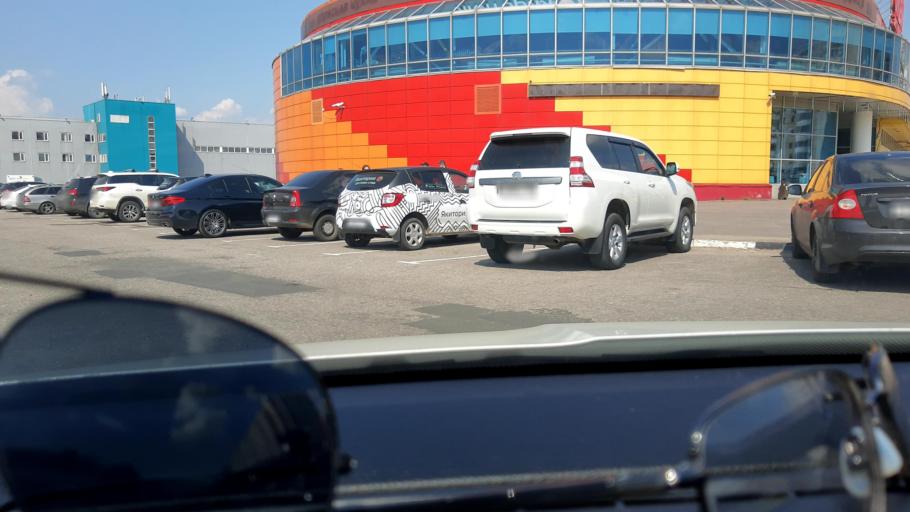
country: RU
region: Moskovskaya
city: Lobnya
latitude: 56.0079
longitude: 37.4384
